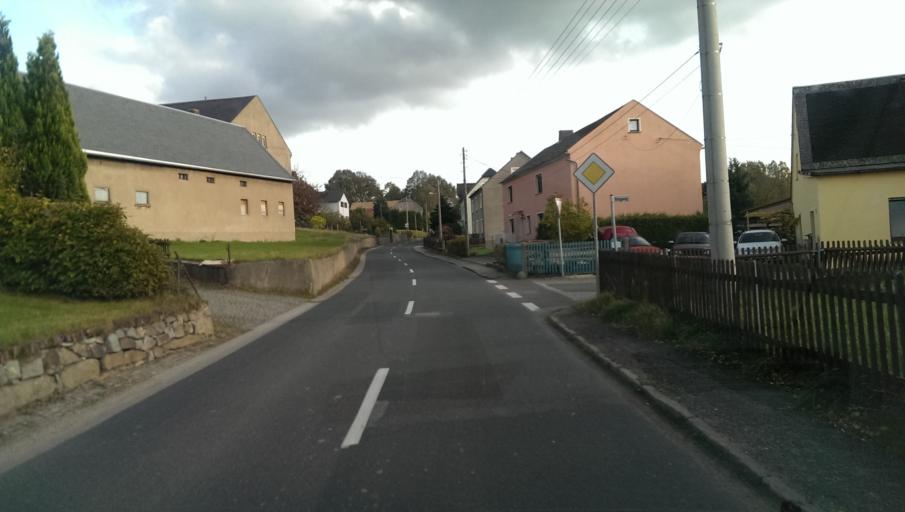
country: DE
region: Saxony
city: Haselbachtal
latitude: 51.2340
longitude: 14.0463
